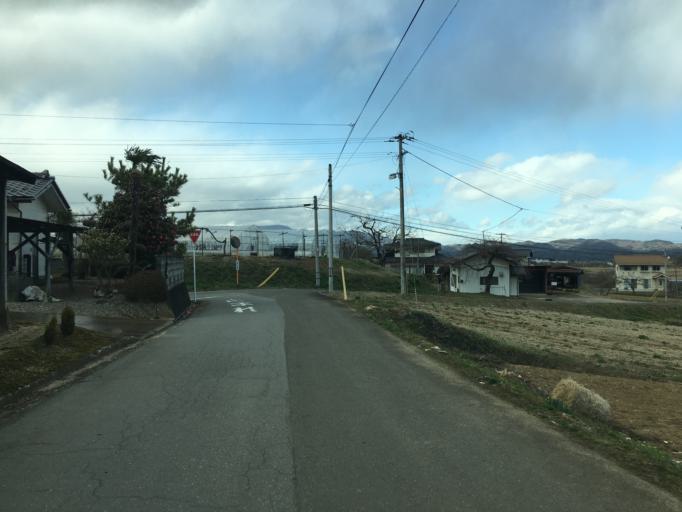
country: JP
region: Fukushima
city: Yanagawamachi-saiwaicho
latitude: 37.8378
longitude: 140.6095
